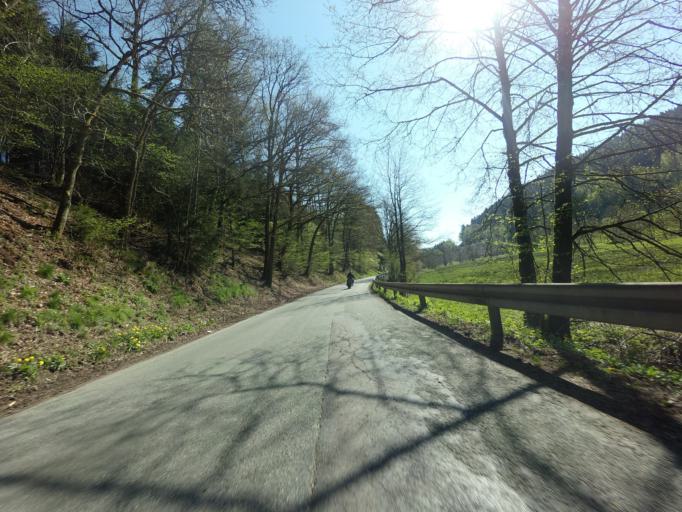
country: DE
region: North Rhine-Westphalia
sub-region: Regierungsbezirk Arnsberg
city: Herscheid
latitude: 51.1034
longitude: 7.7323
